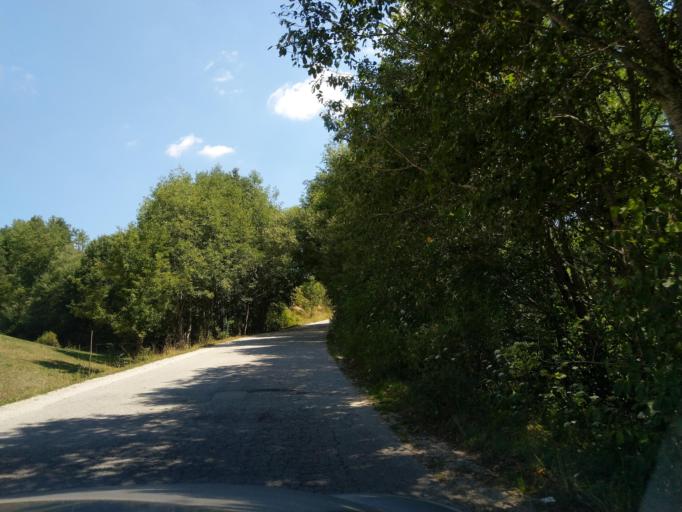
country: RS
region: Central Serbia
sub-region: Zlatiborski Okrug
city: Nova Varos
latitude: 43.4574
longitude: 19.9728
